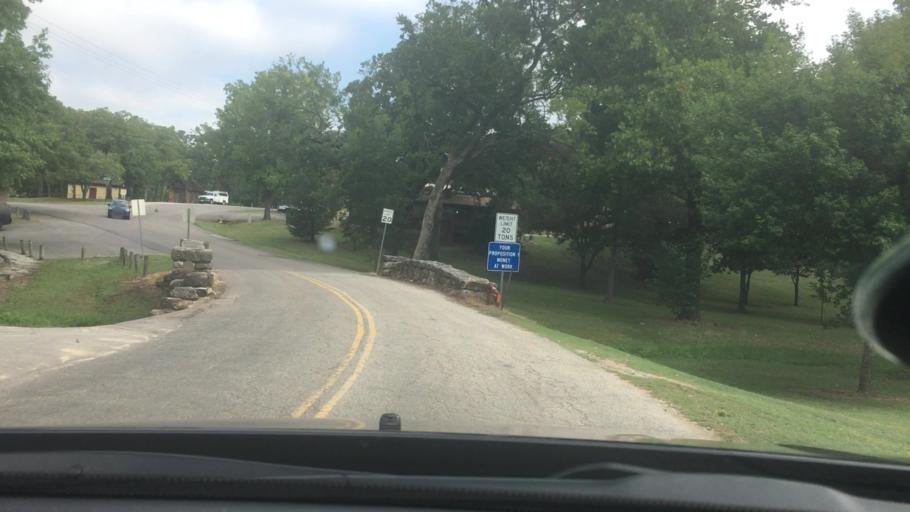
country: US
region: Oklahoma
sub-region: Pontotoc County
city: Ada
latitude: 34.7652
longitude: -96.6520
